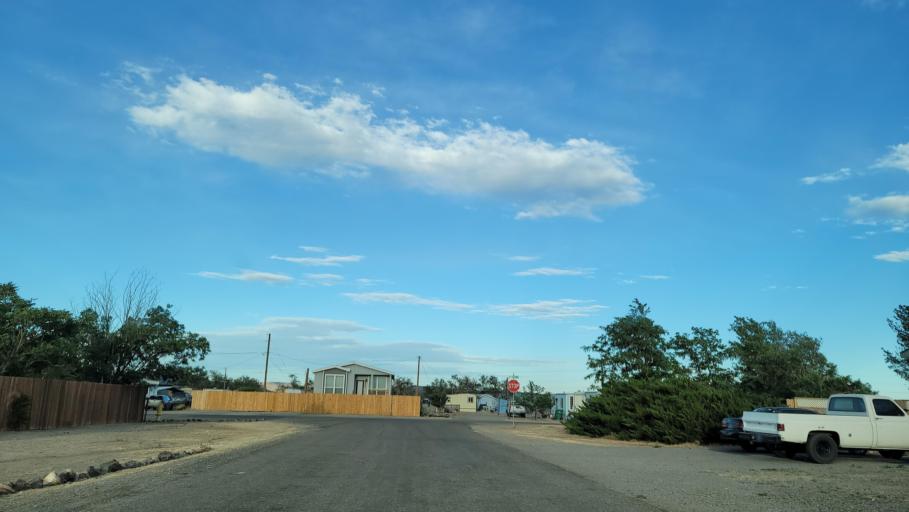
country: US
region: Nevada
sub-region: Lyon County
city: Silver Springs
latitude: 39.4052
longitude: -119.2222
